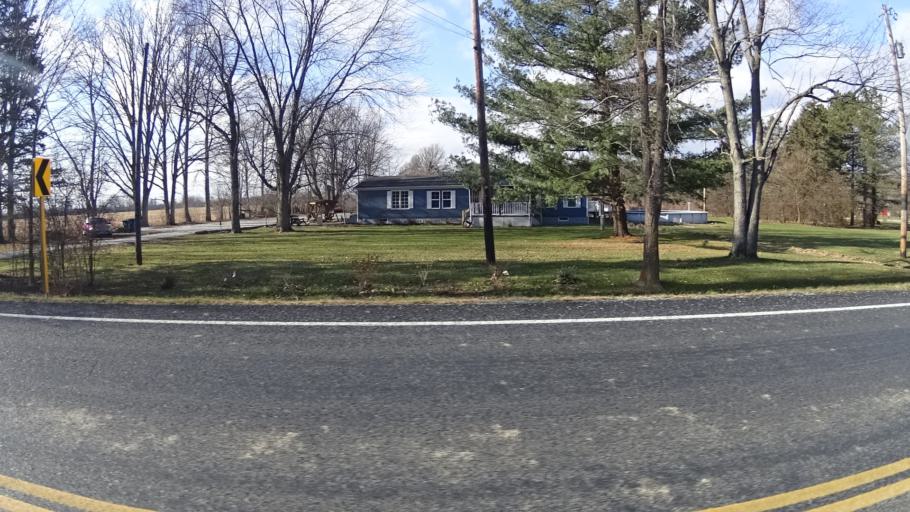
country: US
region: Ohio
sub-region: Lorain County
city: Camden
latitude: 41.2761
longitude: -82.2747
